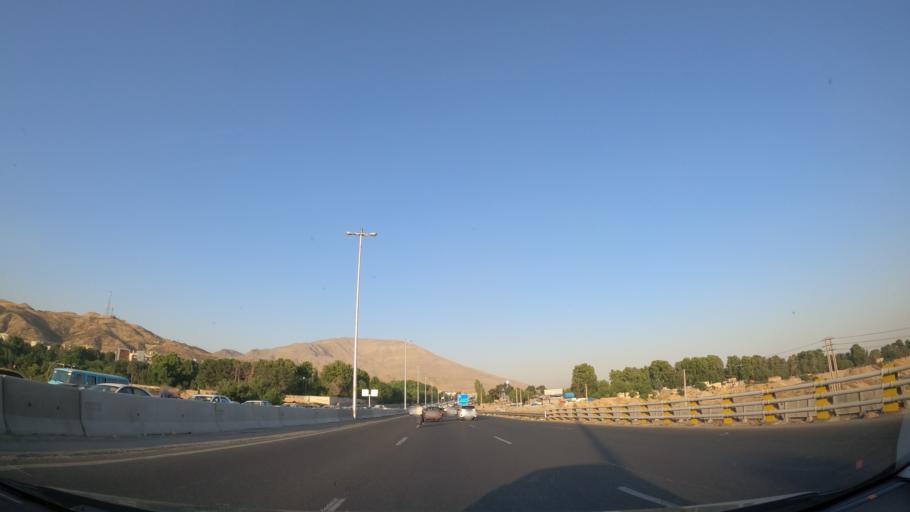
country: IR
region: Alborz
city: Karaj
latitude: 35.7903
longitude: 51.0090
